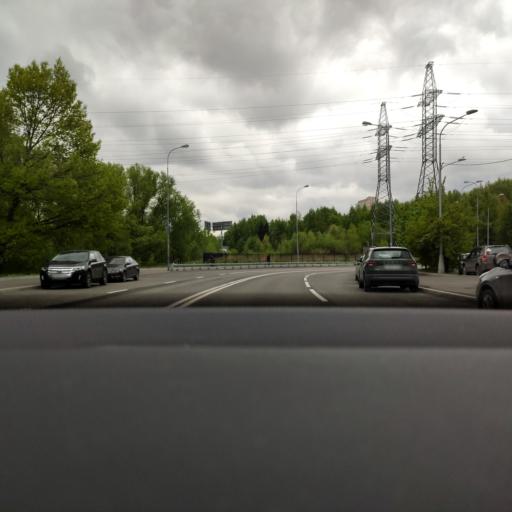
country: RU
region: Moscow
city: Vagonoremont
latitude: 55.9120
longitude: 37.5565
